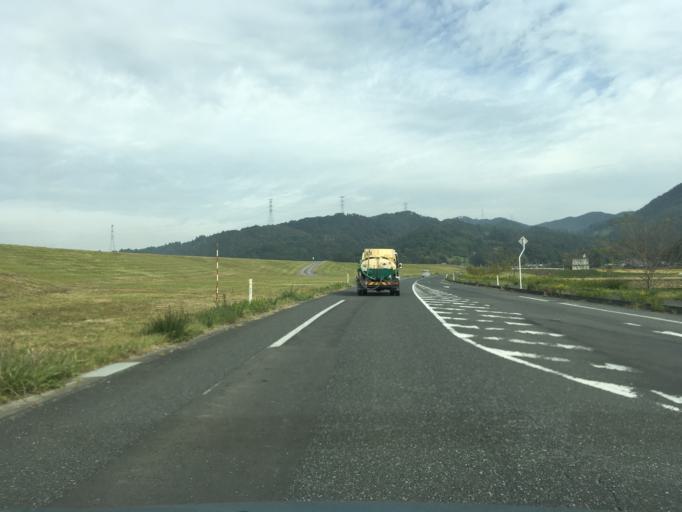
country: JP
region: Iwate
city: Ichinoseki
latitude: 38.9223
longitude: 141.2558
